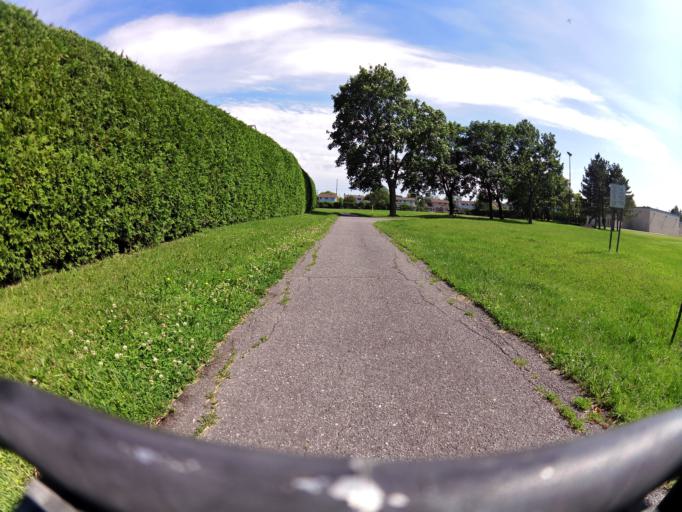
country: CA
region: Ontario
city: Ottawa
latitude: 45.3694
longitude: -75.7113
